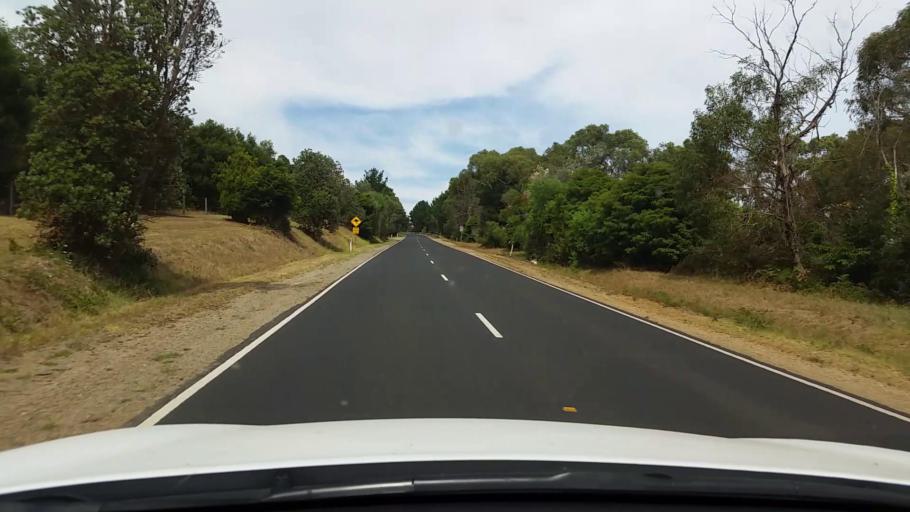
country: AU
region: Victoria
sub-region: Mornington Peninsula
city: Merricks
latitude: -38.4356
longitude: 145.0408
